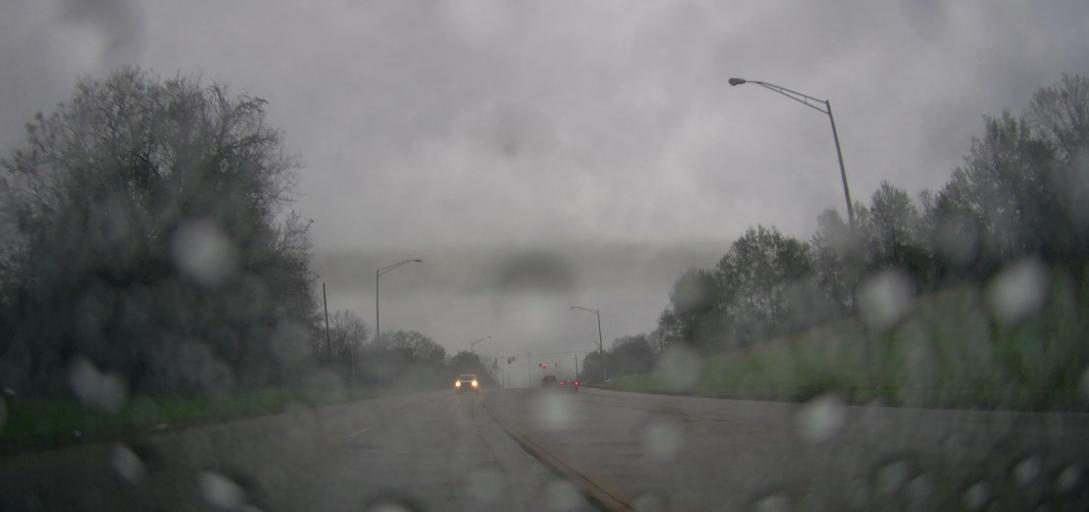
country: US
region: Alabama
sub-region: Montgomery County
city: Montgomery
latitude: 32.3694
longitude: -86.3319
